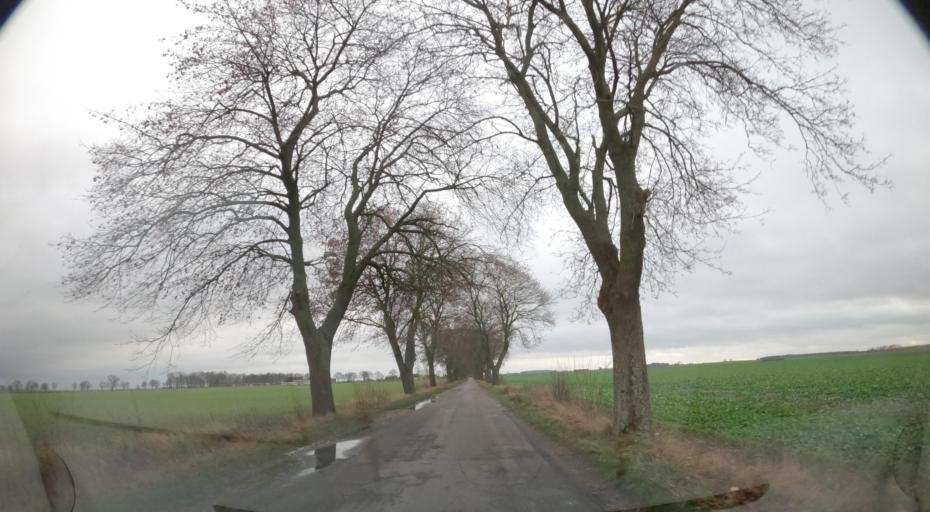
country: PL
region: Greater Poland Voivodeship
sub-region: Powiat pilski
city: Wysoka
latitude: 53.2746
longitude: 17.0990
